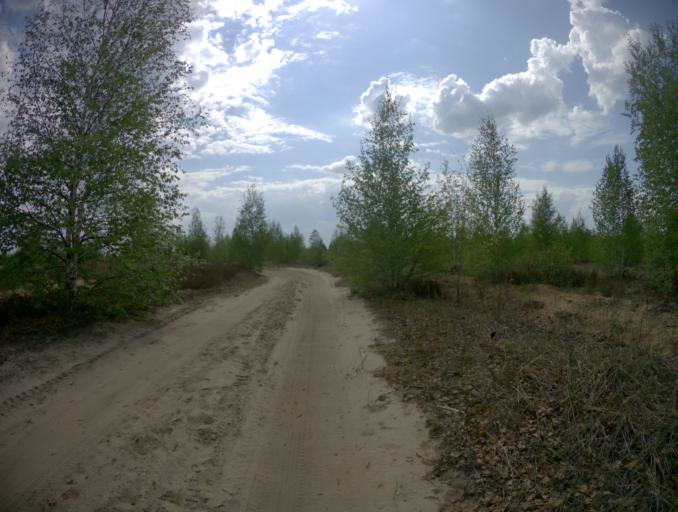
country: RU
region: Ivanovo
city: Talitsy
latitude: 56.4671
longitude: 42.2058
